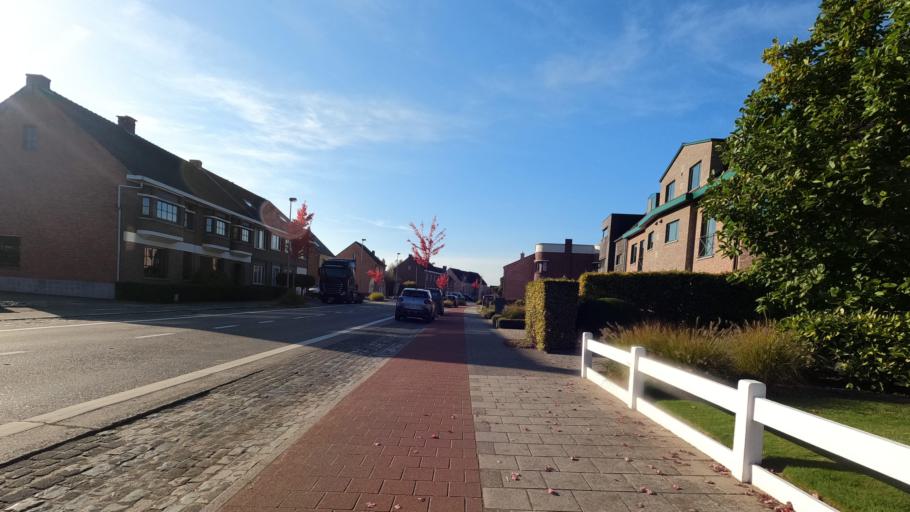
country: BE
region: Flanders
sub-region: Provincie Antwerpen
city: Hulshout
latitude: 51.0516
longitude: 4.7691
